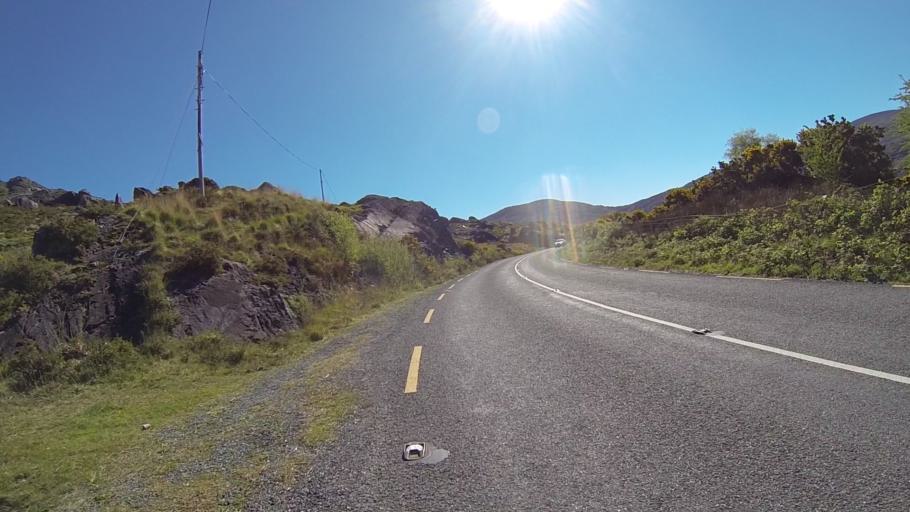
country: IE
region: Munster
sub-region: Ciarrai
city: Kenmare
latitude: 51.7726
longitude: -9.7467
